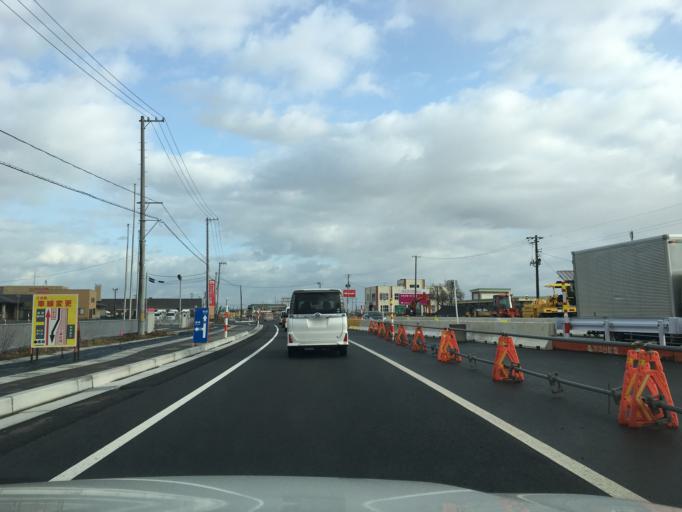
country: JP
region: Yamagata
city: Sakata
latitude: 38.8477
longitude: 139.8486
